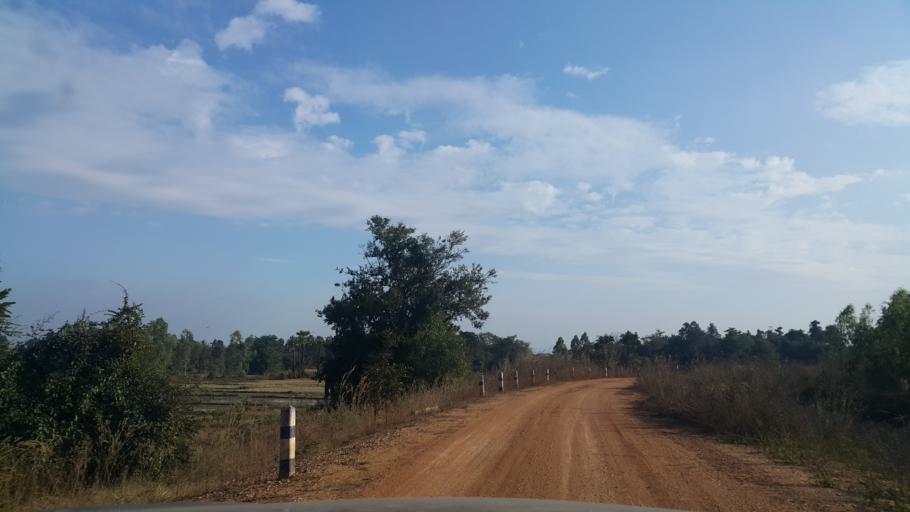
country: TH
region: Lampang
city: Ko Kha
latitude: 18.2562
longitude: 99.3665
